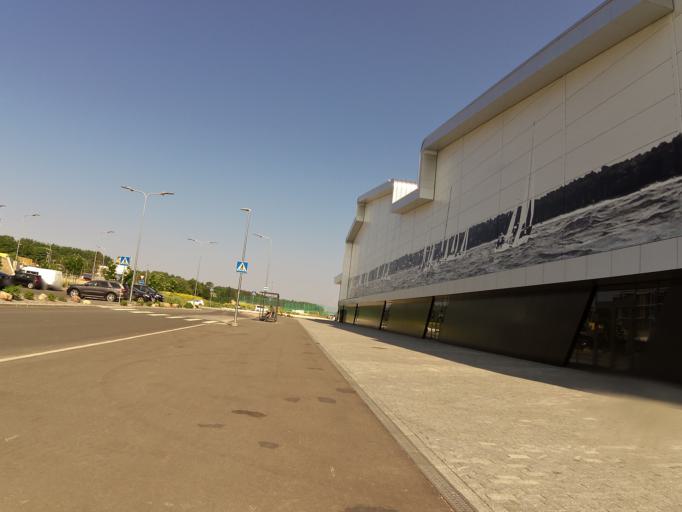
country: EE
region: Harju
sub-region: Harku vald
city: Tabasalu
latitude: 59.4497
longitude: 24.6055
